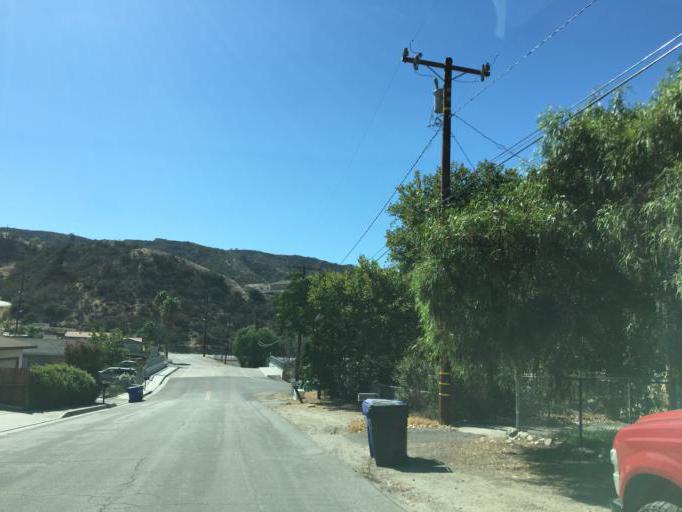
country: US
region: California
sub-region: Los Angeles County
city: Agua Dulce
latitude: 34.4468
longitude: -118.4289
